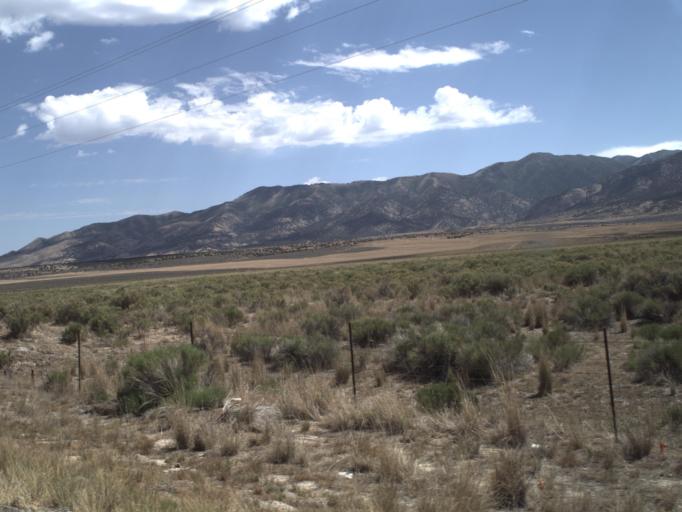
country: US
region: Utah
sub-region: Tooele County
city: Tooele
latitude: 40.3847
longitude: -112.3864
